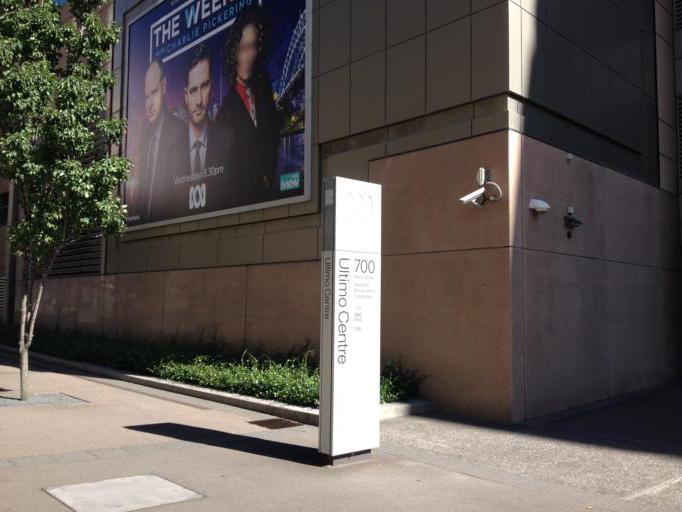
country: AU
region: New South Wales
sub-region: City of Sydney
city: Haberfield
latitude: -33.8821
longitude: 151.2023
